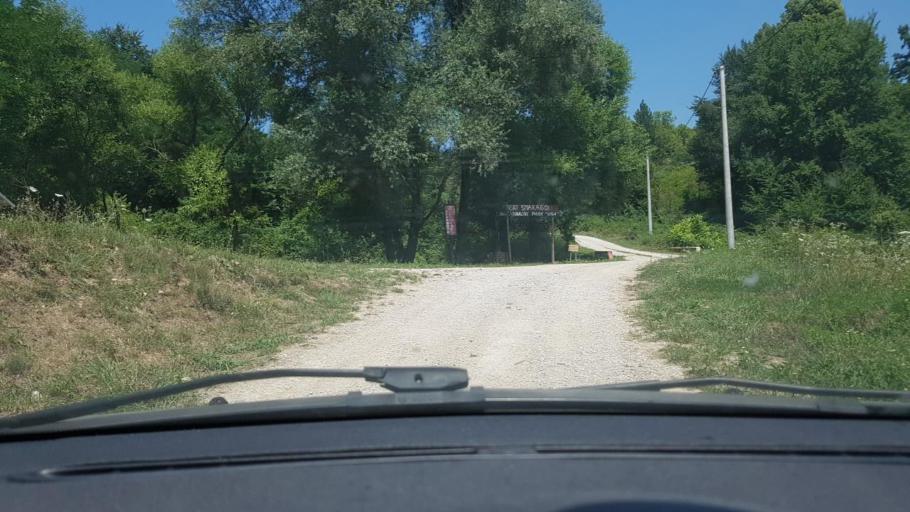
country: BA
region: Federation of Bosnia and Herzegovina
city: Orasac
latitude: 44.5674
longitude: 16.0793
